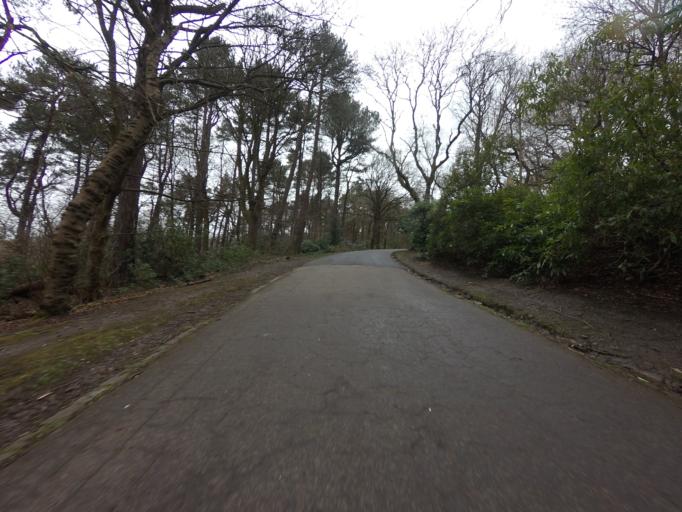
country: GB
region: Scotland
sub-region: East Renfrewshire
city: Giffnock
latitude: 55.8330
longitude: -4.3141
